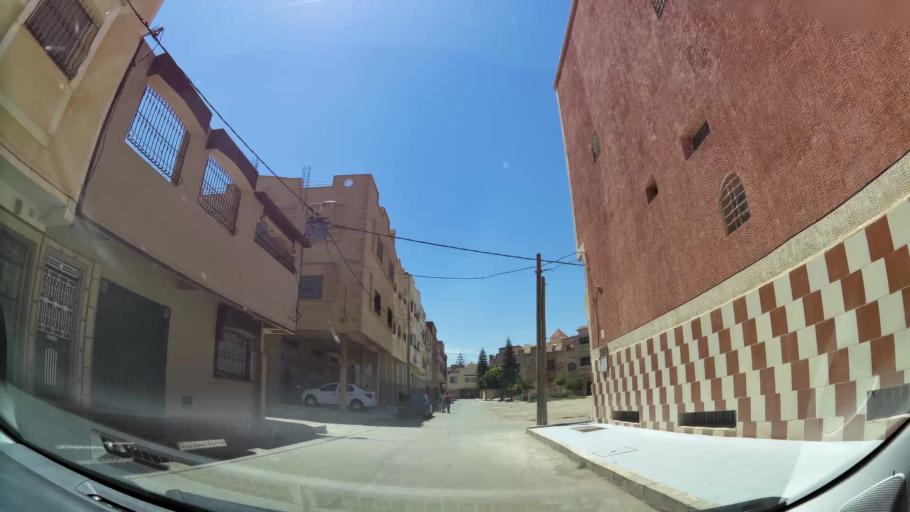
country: MA
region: Oriental
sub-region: Oujda-Angad
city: Oujda
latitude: 34.6673
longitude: -1.8901
